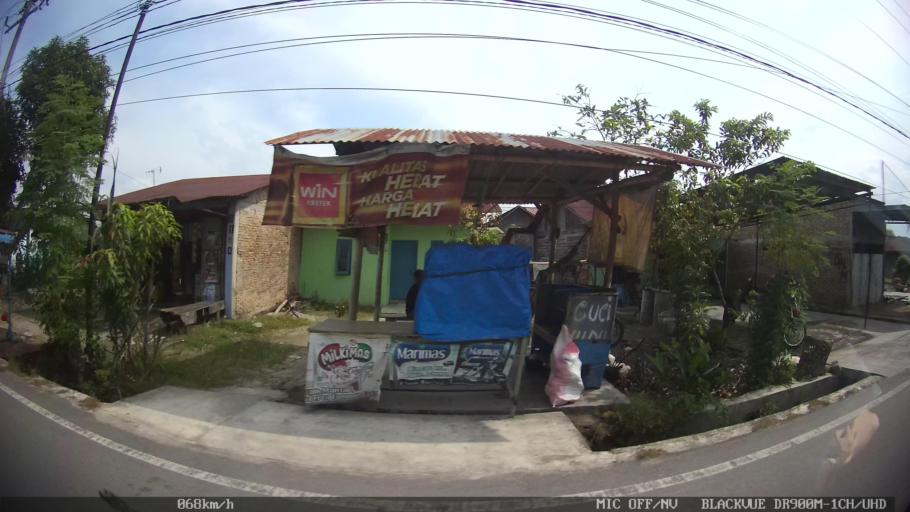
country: ID
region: North Sumatra
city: Percut
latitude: 3.6118
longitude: 98.8144
